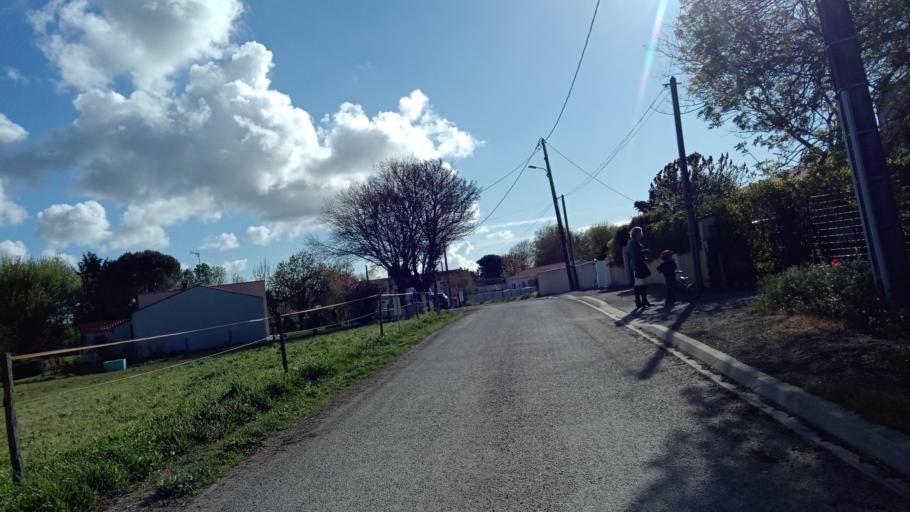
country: FR
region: Poitou-Charentes
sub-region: Departement de la Charente-Maritime
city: Verines
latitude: 46.1675
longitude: -0.9466
